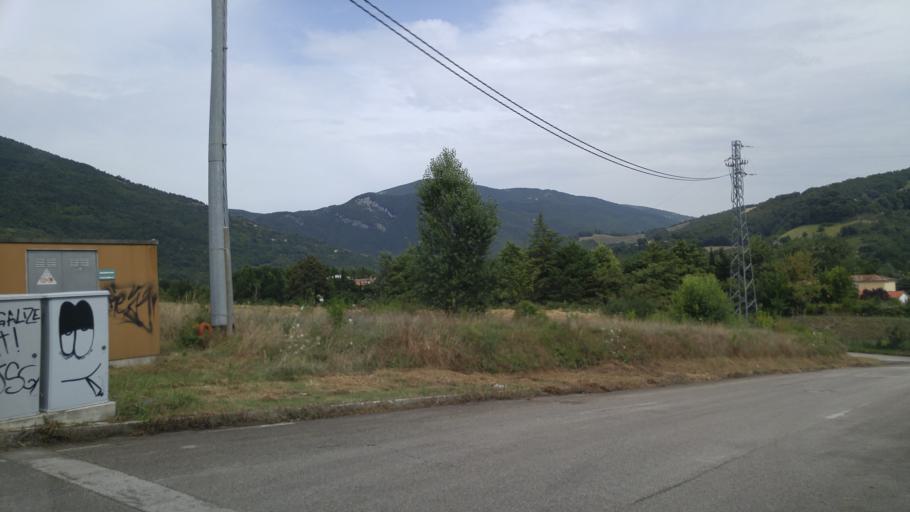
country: IT
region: The Marches
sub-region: Provincia di Pesaro e Urbino
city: Acqualagna
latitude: 43.6354
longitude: 12.6851
